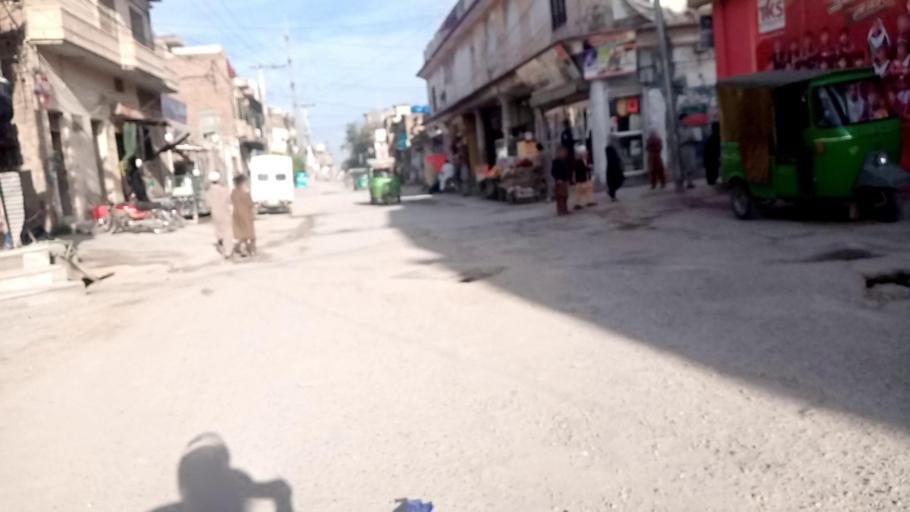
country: PK
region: Khyber Pakhtunkhwa
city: Peshawar
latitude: 34.0120
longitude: 71.6092
